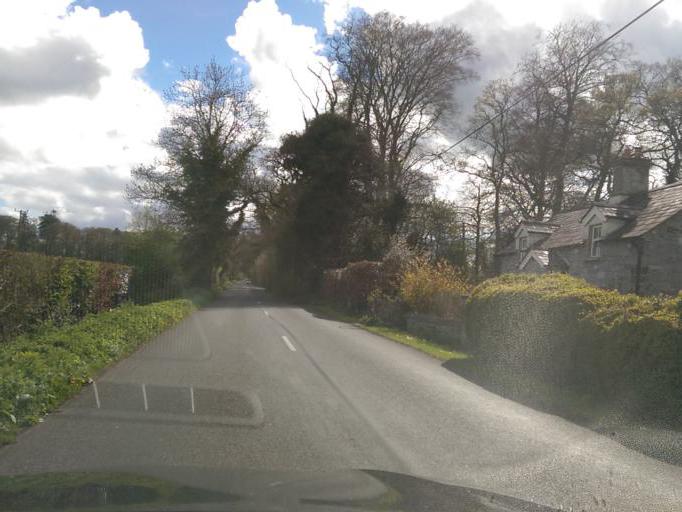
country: IE
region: Leinster
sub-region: An Mhi
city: Dunshaughlin
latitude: 53.5306
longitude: -6.6371
